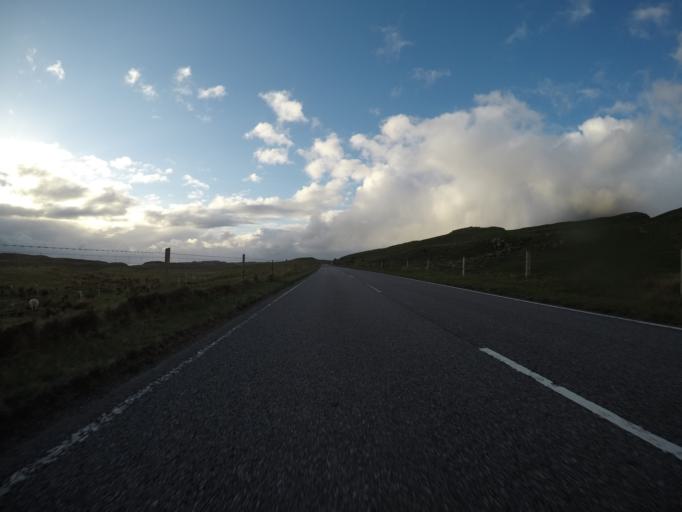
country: GB
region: Scotland
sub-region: Highland
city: Portree
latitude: 57.5392
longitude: -6.3629
